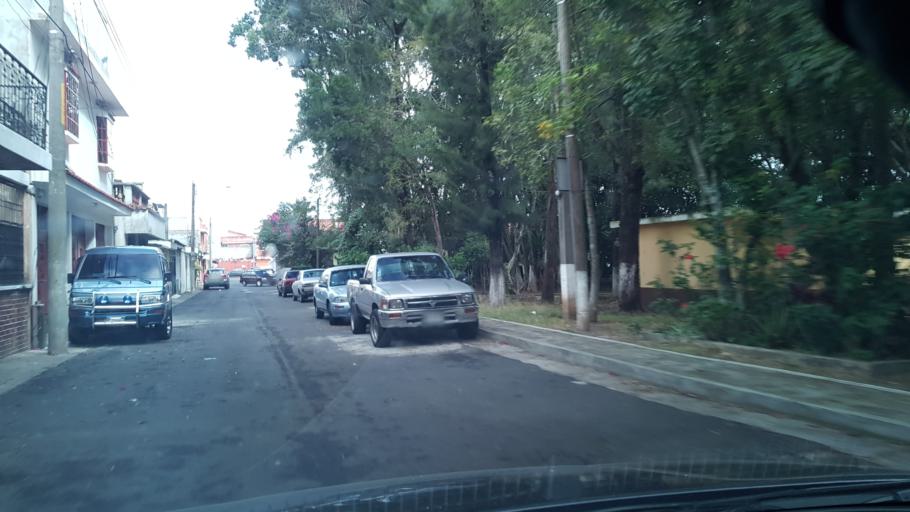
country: GT
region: Guatemala
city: Mixco
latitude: 14.6395
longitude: -90.5762
